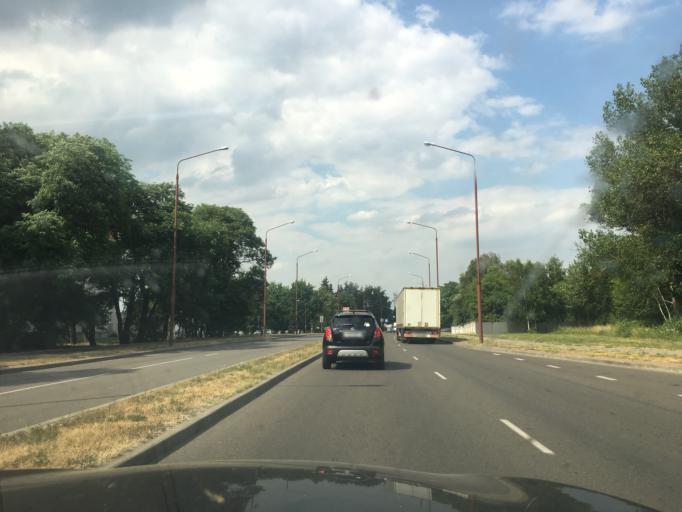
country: BY
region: Brest
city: Brest
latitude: 52.1367
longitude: 23.6758
